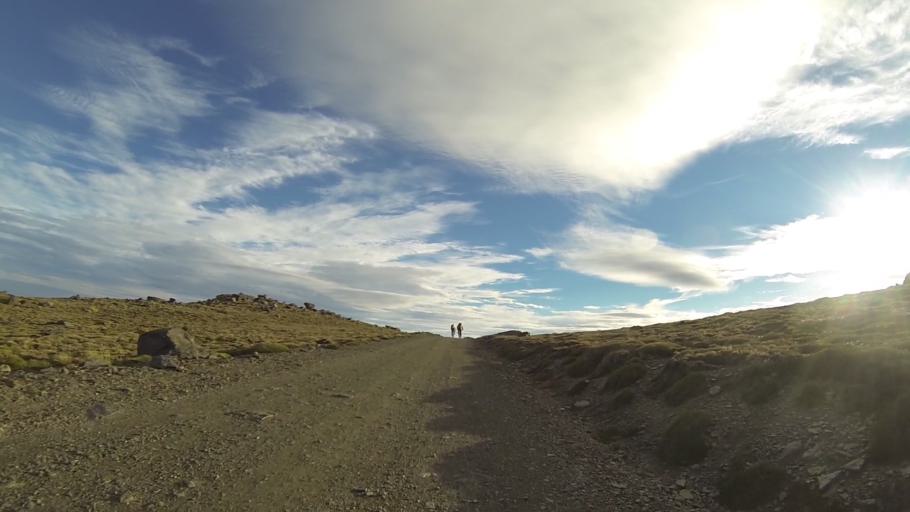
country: ES
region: Andalusia
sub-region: Provincia de Granada
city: Trevelez
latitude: 37.0001
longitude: -3.3102
